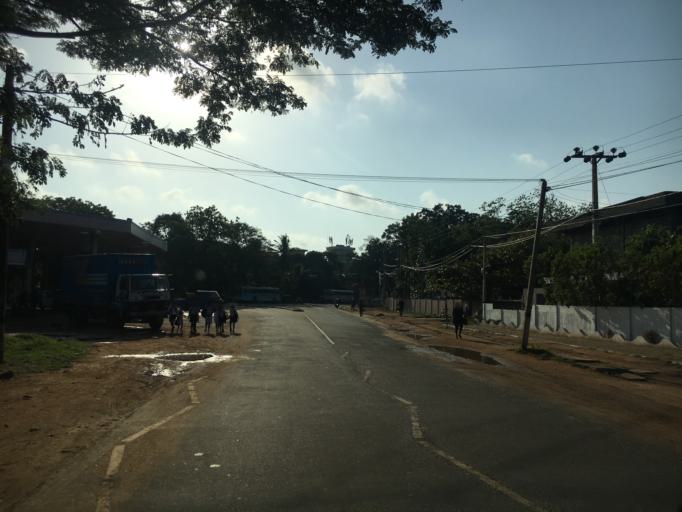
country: LK
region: Northern Province
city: Vavuniya
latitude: 8.7613
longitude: 80.4978
